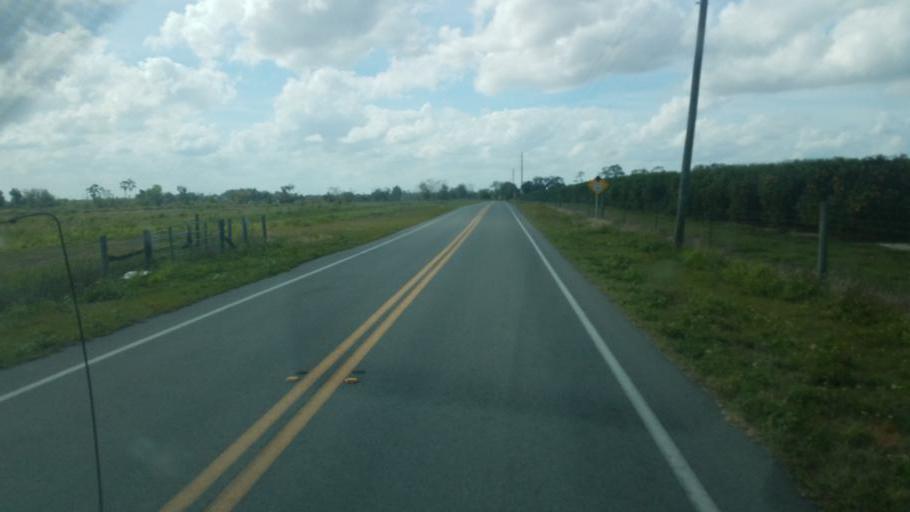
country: US
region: Florida
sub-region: Polk County
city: Babson Park
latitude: 27.9252
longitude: -81.4792
